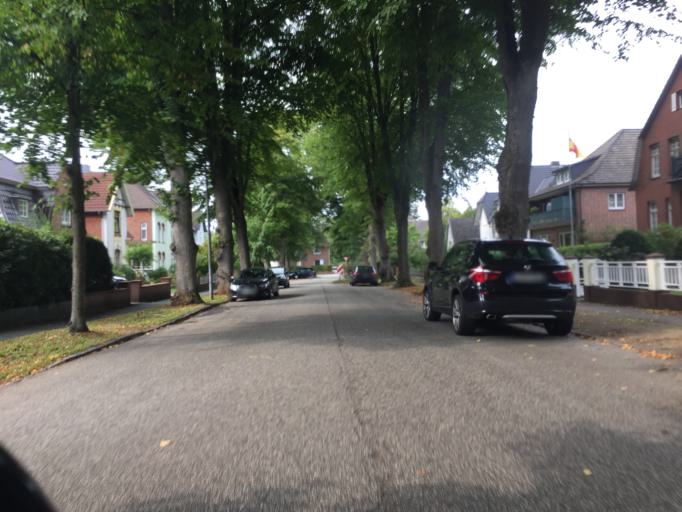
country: DE
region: Schleswig-Holstein
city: Itzehoe
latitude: 53.9346
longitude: 9.5095
